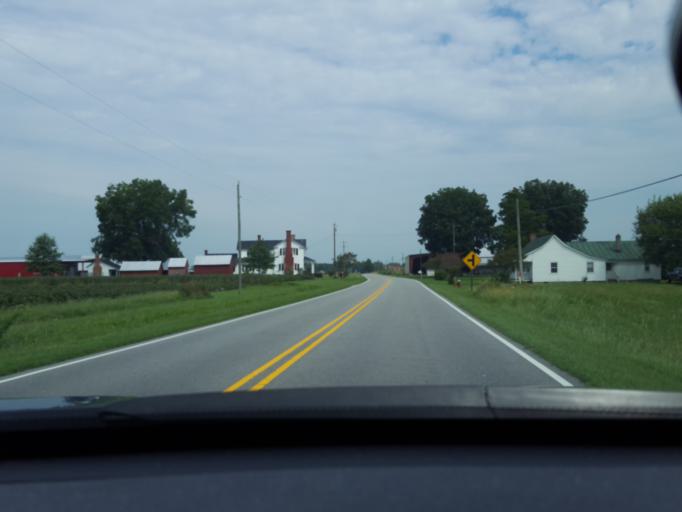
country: US
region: North Carolina
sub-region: Chowan County
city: Edenton
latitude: 36.1893
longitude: -76.6611
